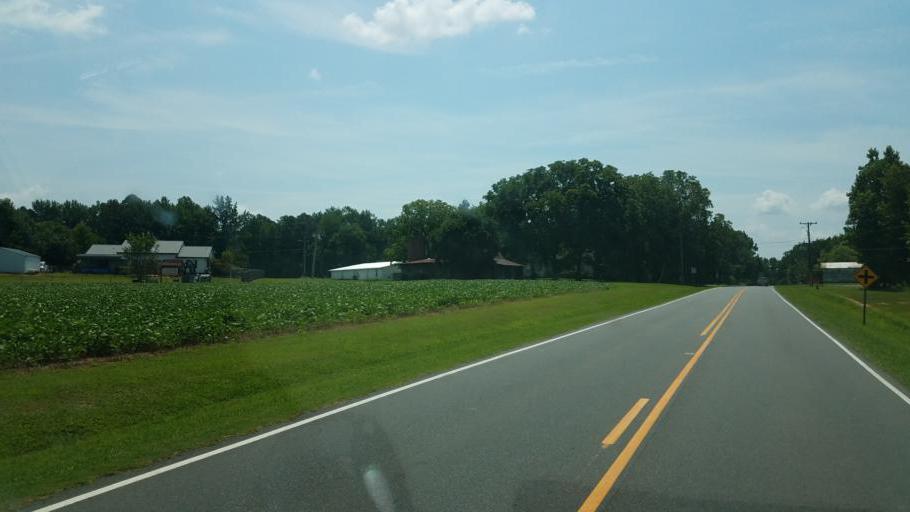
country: US
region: North Carolina
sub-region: Gaston County
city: Tryon
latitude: 35.3503
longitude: -81.3515
